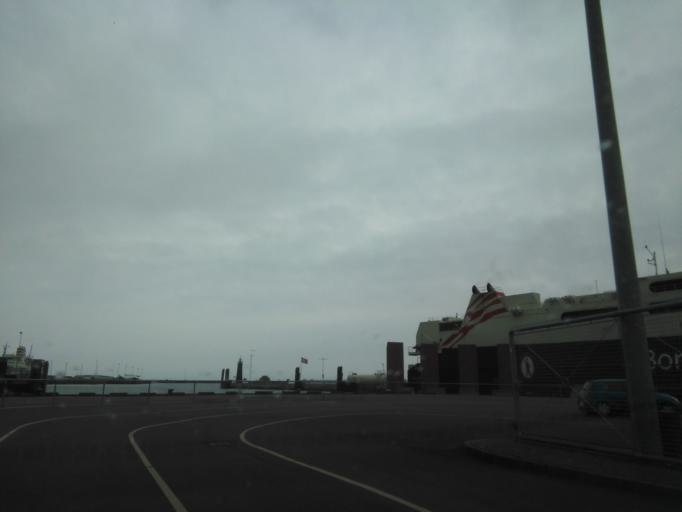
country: DK
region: Capital Region
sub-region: Bornholm Kommune
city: Ronne
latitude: 55.0995
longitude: 14.6927
